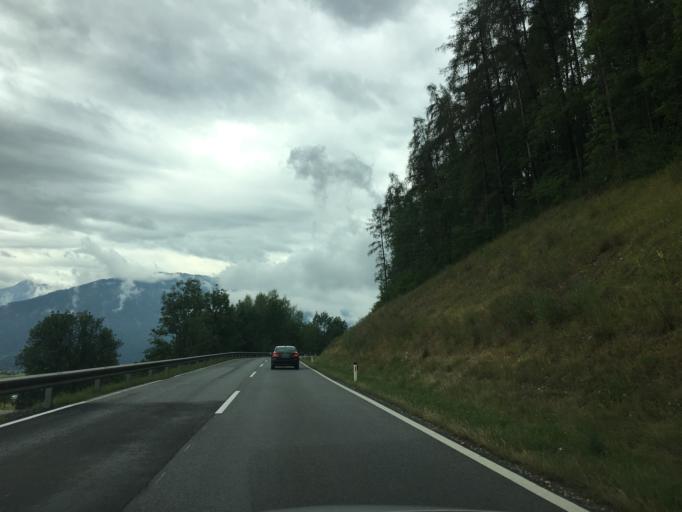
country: AT
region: Tyrol
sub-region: Politischer Bezirk Imst
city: Tarrenz
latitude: 47.2583
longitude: 10.7540
